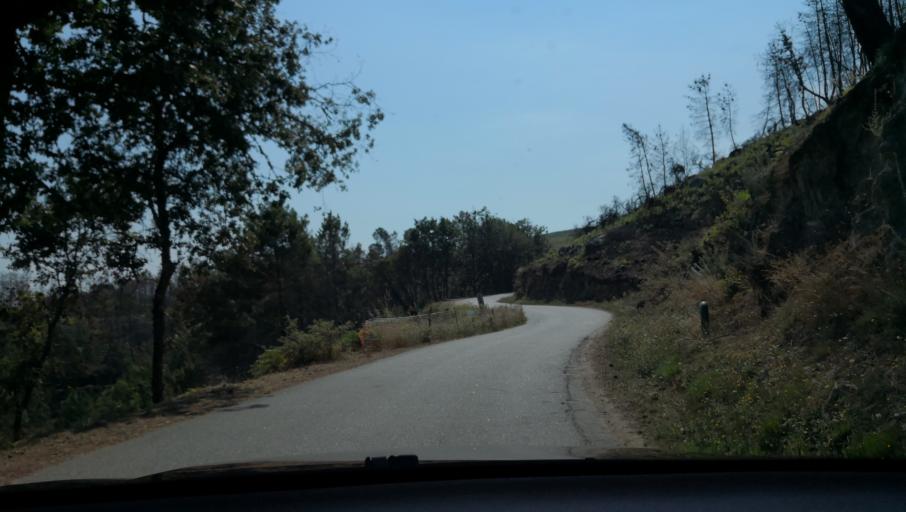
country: PT
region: Vila Real
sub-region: Sabrosa
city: Sabrosa
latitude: 41.3430
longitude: -7.5959
